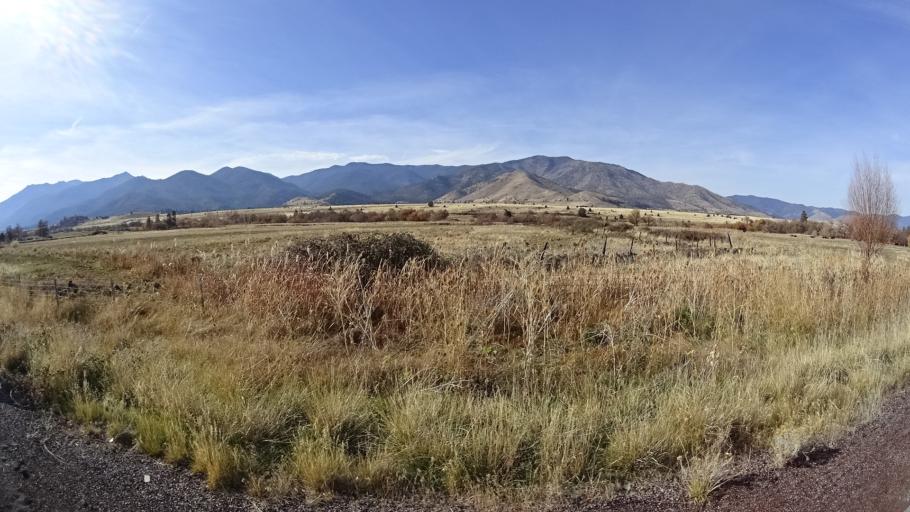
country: US
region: California
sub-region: Siskiyou County
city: Weed
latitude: 41.4691
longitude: -122.4350
